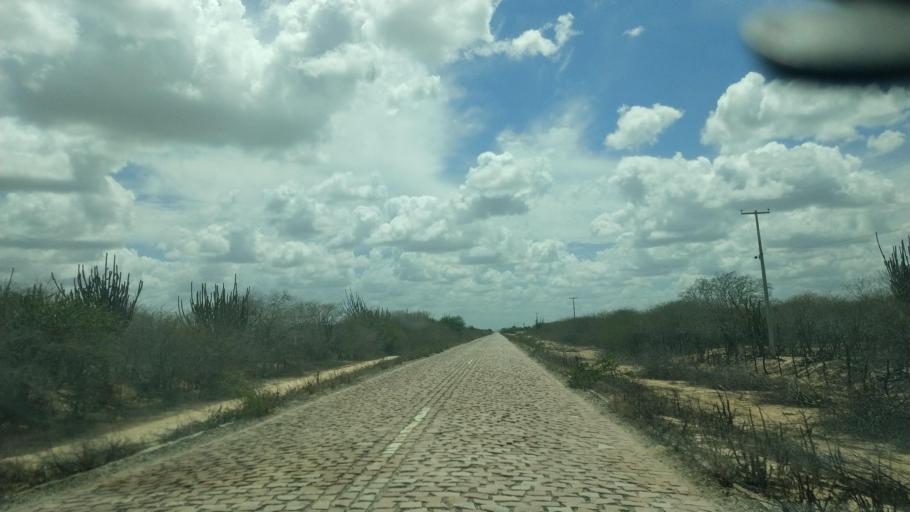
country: BR
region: Rio Grande do Norte
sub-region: Sao Paulo Do Potengi
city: Sao Paulo do Potengi
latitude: -5.9662
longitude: -35.8515
